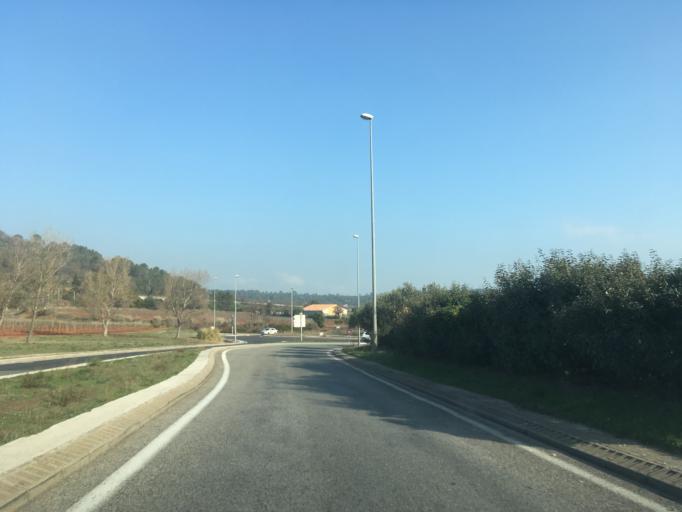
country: FR
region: Provence-Alpes-Cote d'Azur
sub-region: Departement du Var
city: Le Cannet-des-Maures
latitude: 43.3929
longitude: 6.3496
